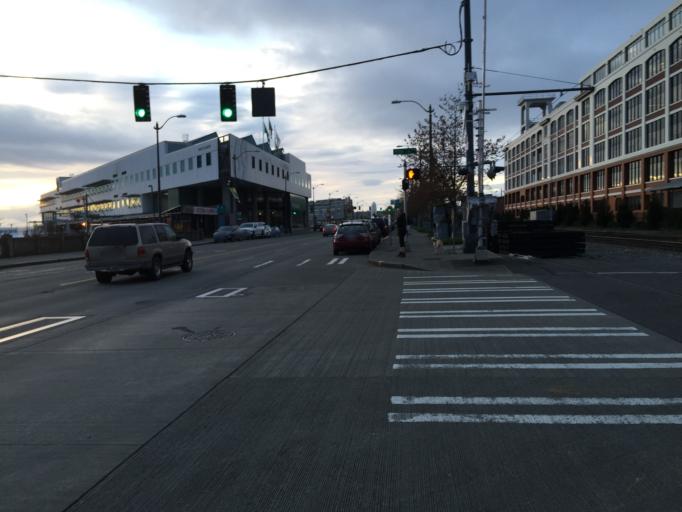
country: US
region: Washington
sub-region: King County
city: Seattle
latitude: 47.6134
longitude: -122.3519
